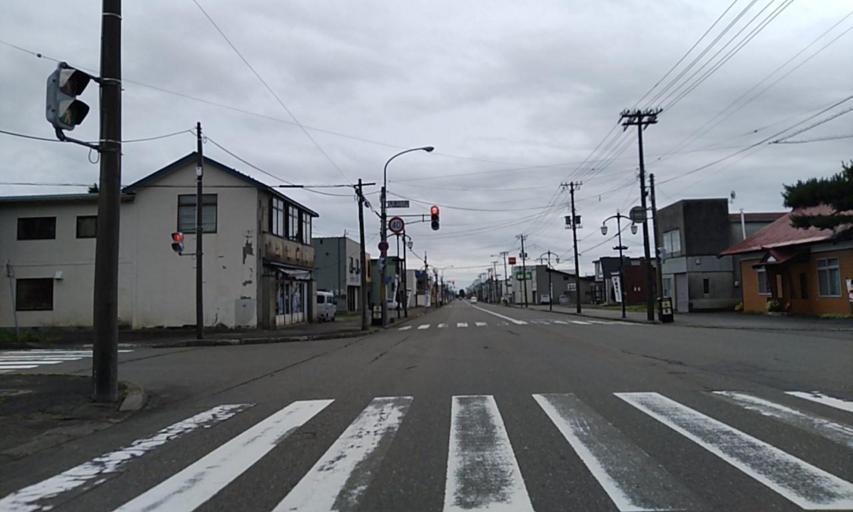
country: JP
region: Hokkaido
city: Obihiro
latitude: 42.2915
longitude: 143.3133
